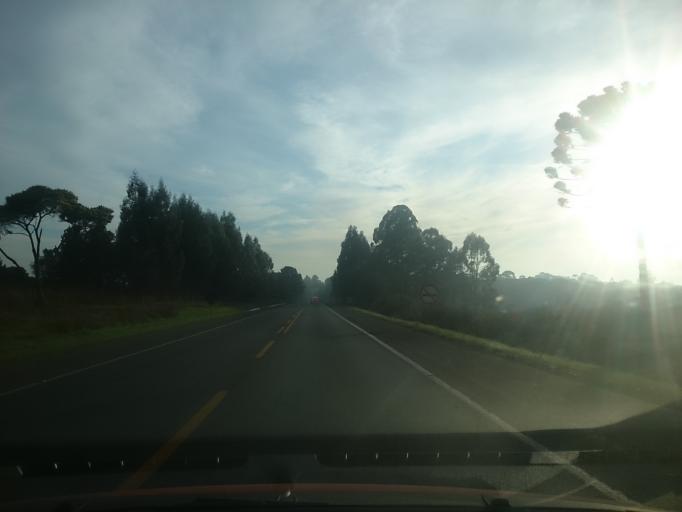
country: BR
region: Rio Grande do Sul
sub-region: Vacaria
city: Estrela
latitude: -28.2776
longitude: -50.7982
